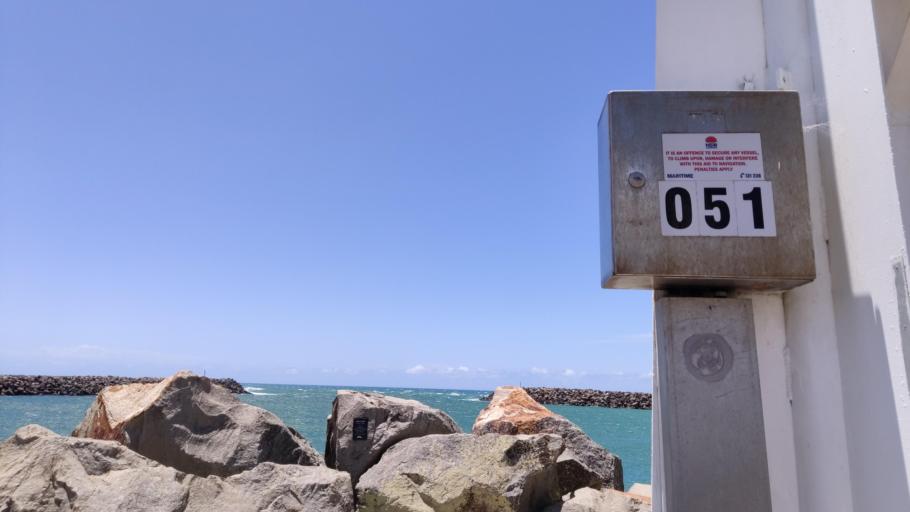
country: AU
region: New South Wales
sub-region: Port Macquarie-Hastings
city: North Haven
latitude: -31.6373
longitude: 152.8342
